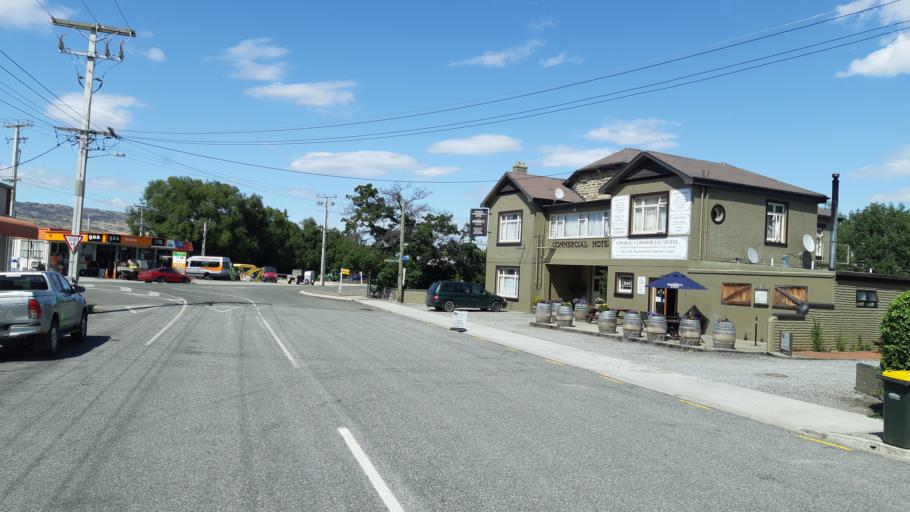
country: NZ
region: Otago
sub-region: Queenstown-Lakes District
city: Wanaka
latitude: -45.0936
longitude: 169.6019
